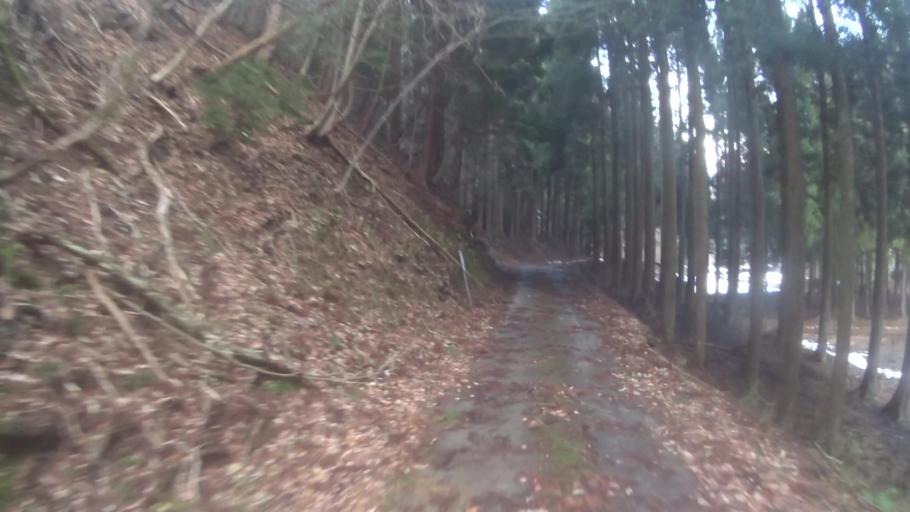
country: JP
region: Kyoto
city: Maizuru
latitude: 35.3997
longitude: 135.5009
